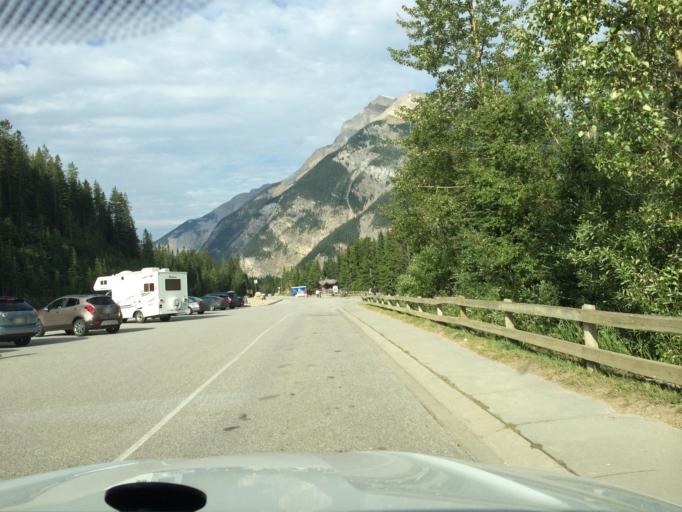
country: CA
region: Alberta
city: Lake Louise
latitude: 51.4314
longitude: -116.4020
